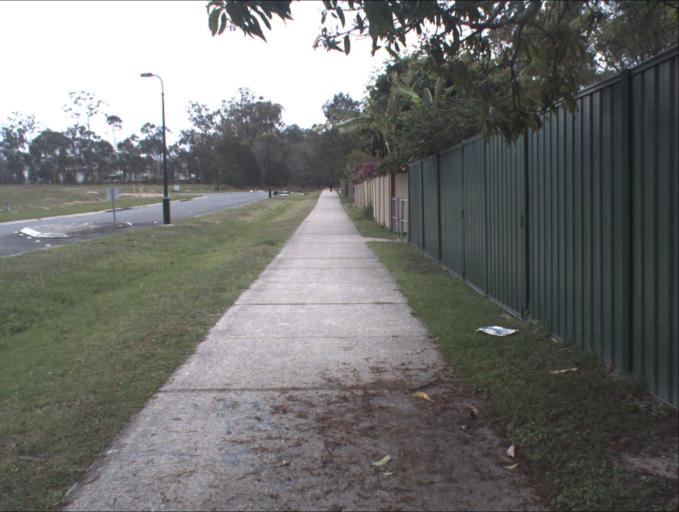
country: AU
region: Queensland
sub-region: Logan
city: Logan Reserve
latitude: -27.6929
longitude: 153.0780
